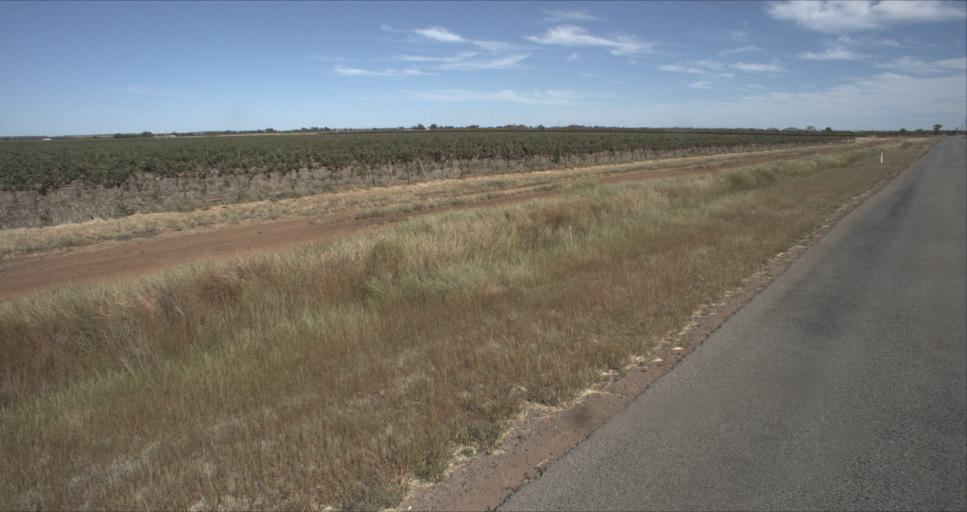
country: AU
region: New South Wales
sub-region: Leeton
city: Leeton
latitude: -34.5799
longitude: 146.3800
